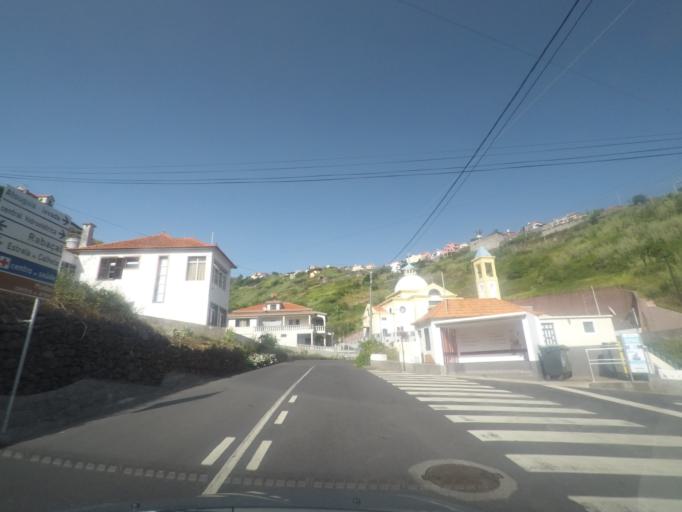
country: PT
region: Madeira
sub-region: Calheta
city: Arco da Calheta
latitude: 32.7297
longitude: -17.1603
